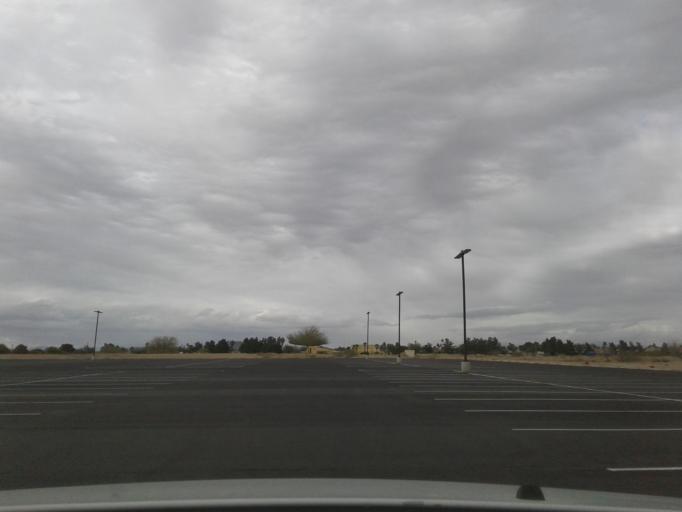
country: US
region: Arizona
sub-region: Maricopa County
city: Glendale
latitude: 33.6062
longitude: -112.1563
